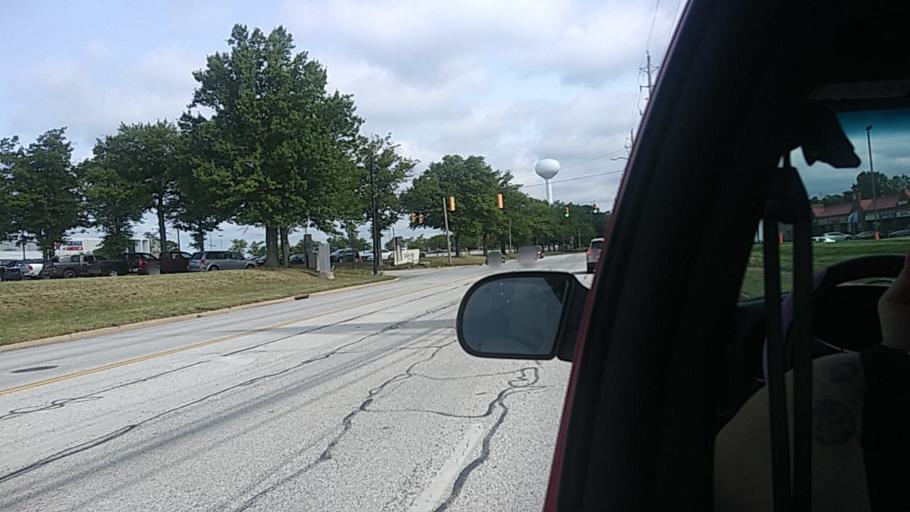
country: US
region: Ohio
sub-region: Summit County
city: Tallmadge
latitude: 41.1137
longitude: -81.4659
